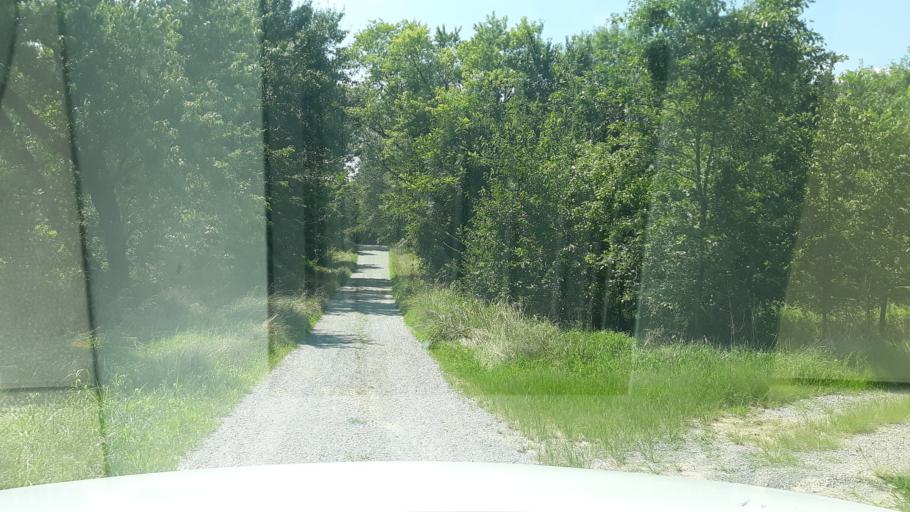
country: US
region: Illinois
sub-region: Saline County
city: Harrisburg
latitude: 37.8524
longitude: -88.6081
